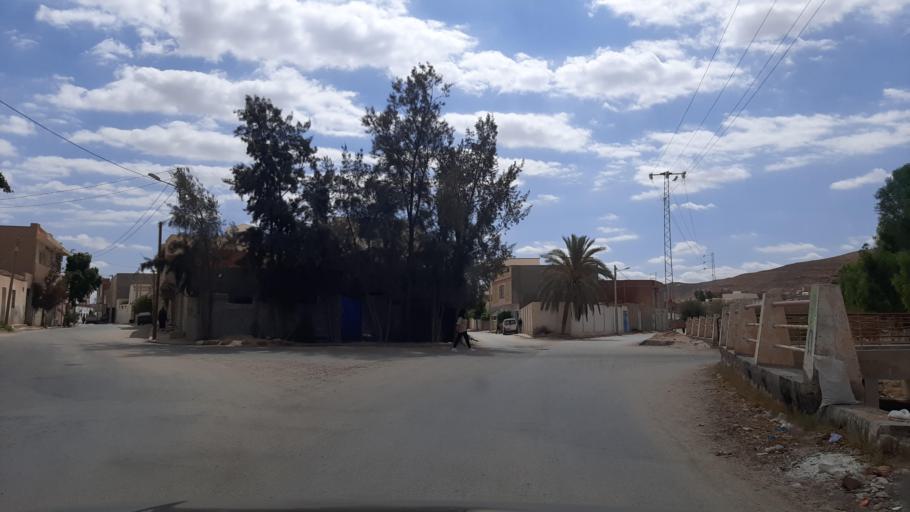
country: TN
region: Tataouine
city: Tataouine
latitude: 32.9286
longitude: 10.4580
